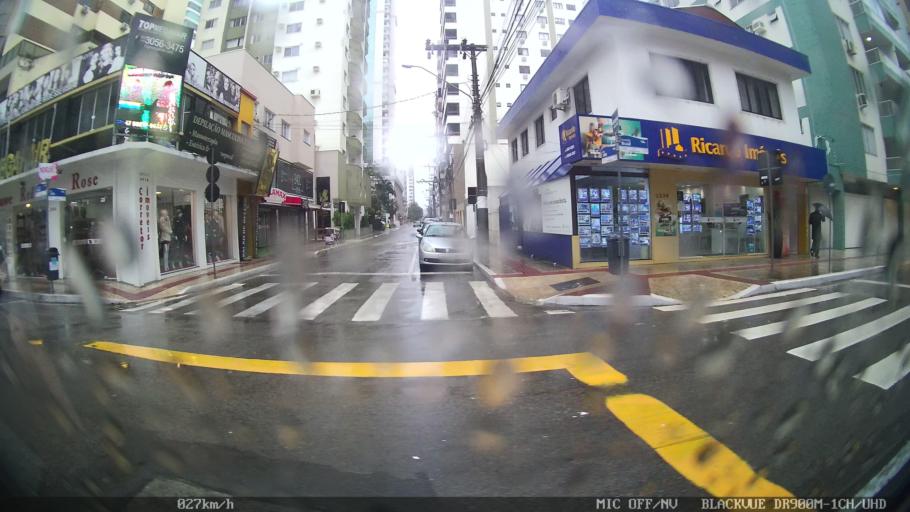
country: BR
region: Santa Catarina
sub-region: Balneario Camboriu
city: Balneario Camboriu
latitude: -26.9937
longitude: -48.6296
